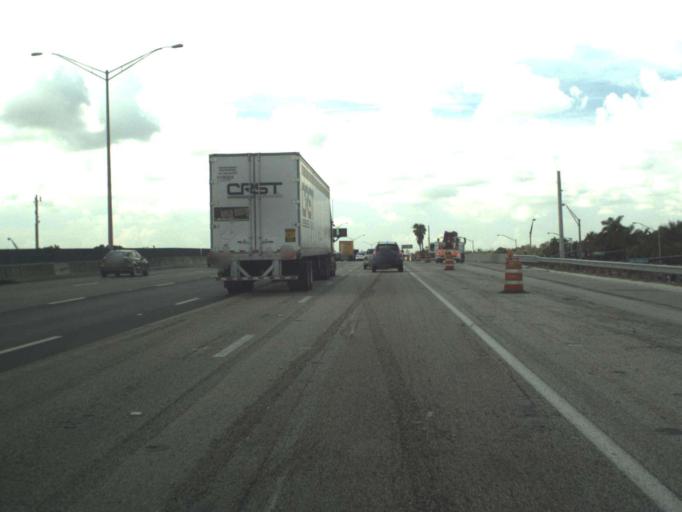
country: US
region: Florida
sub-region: Broward County
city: Hollywood
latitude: 26.0120
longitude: -80.1670
